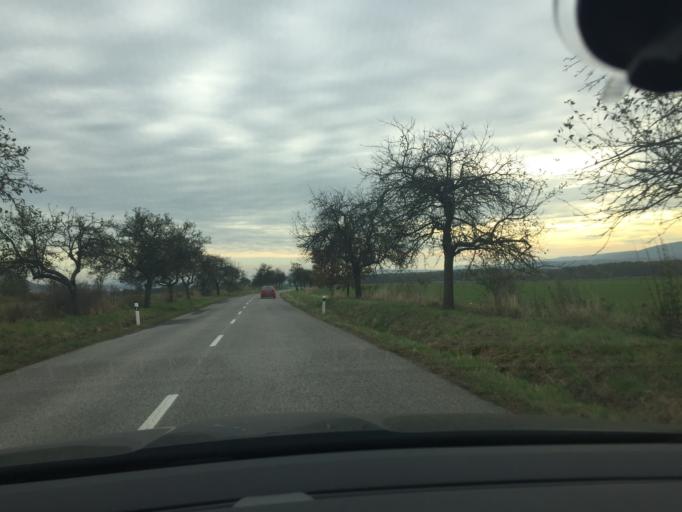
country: SK
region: Presovsky
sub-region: Okres Presov
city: Presov
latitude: 48.9289
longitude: 21.3183
